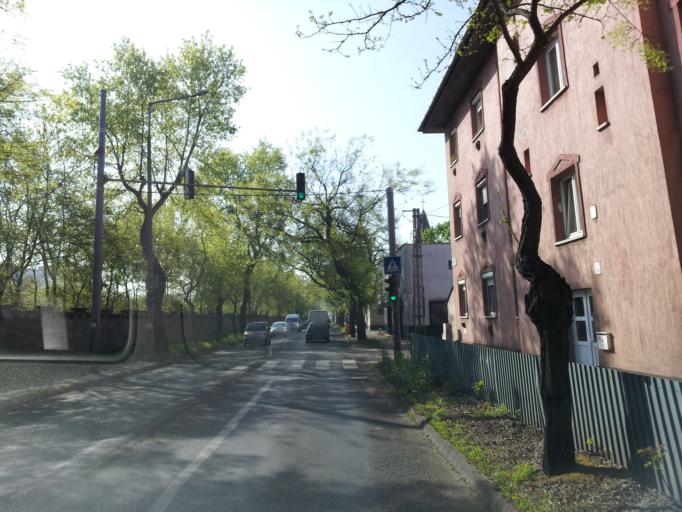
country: HU
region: Budapest
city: Budapest X. keruelet
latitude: 47.4867
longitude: 19.1242
